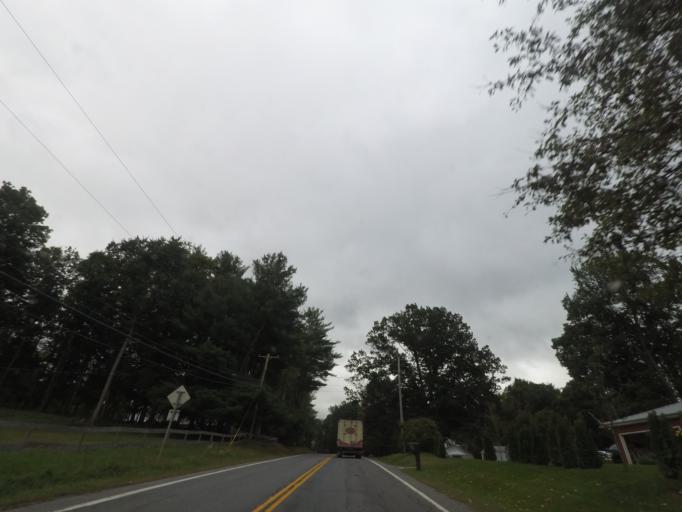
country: US
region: New York
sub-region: Rensselaer County
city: Hoosick Falls
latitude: 42.9301
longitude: -73.3484
